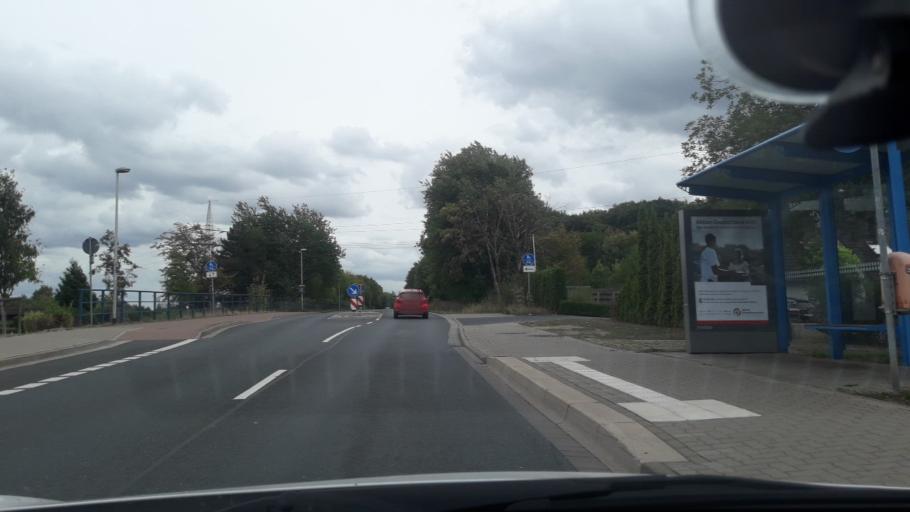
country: DE
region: Lower Saxony
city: Elbe
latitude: 52.1024
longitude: 10.3616
